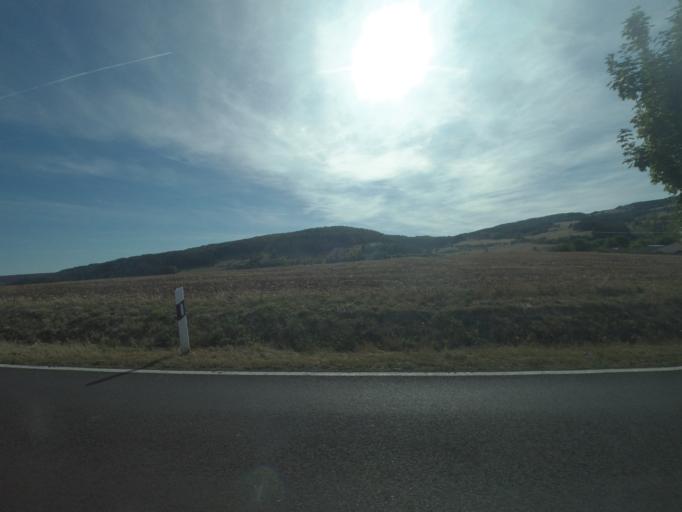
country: DE
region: Thuringia
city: Stepfershausen
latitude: 50.5926
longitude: 10.3094
